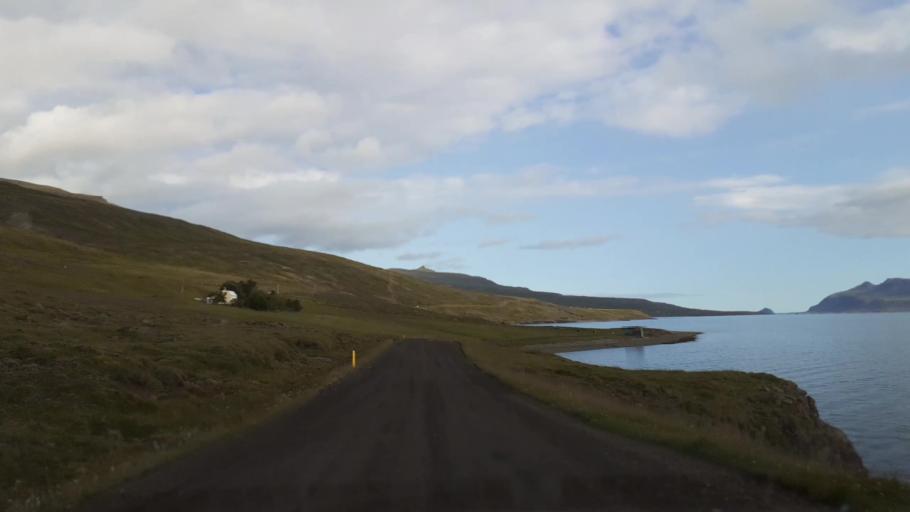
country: IS
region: East
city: Eskifjoerdur
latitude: 65.0384
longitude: -13.8810
